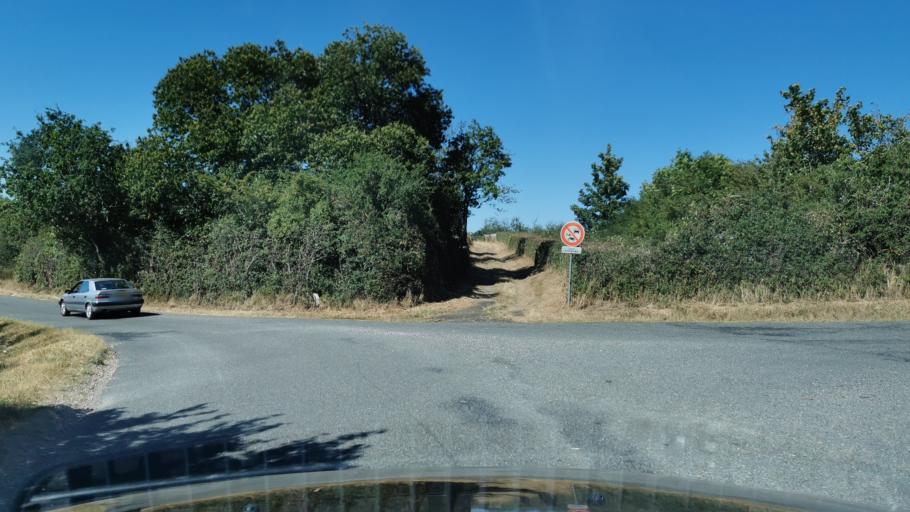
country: FR
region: Bourgogne
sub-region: Departement de Saone-et-Loire
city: Montcenis
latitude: 46.8037
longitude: 4.3939
